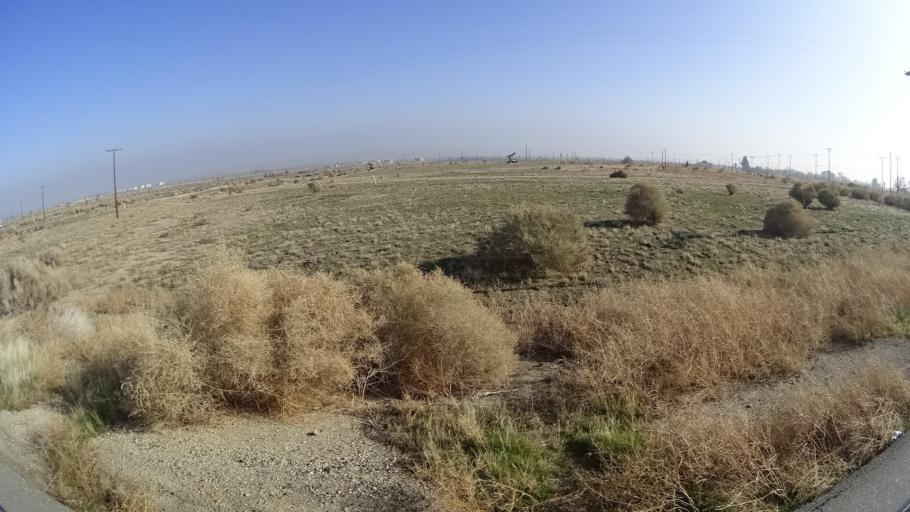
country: US
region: California
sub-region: Kern County
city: Taft Heights
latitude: 35.1806
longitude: -119.5498
